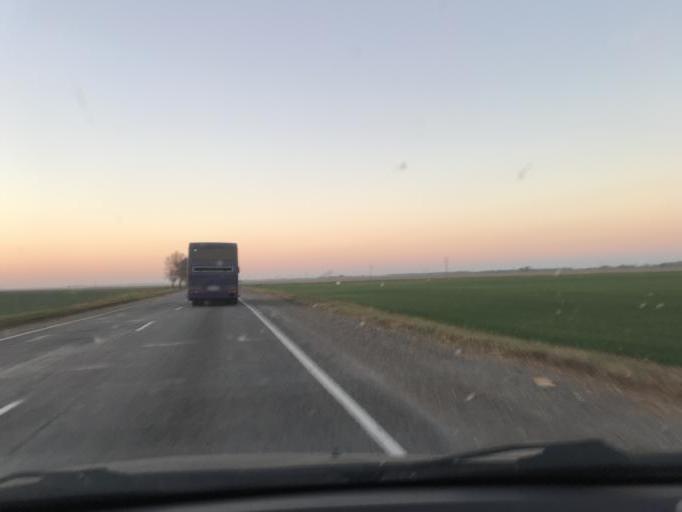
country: BY
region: Gomel
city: Horad Rechytsa
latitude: 52.2198
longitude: 30.5215
